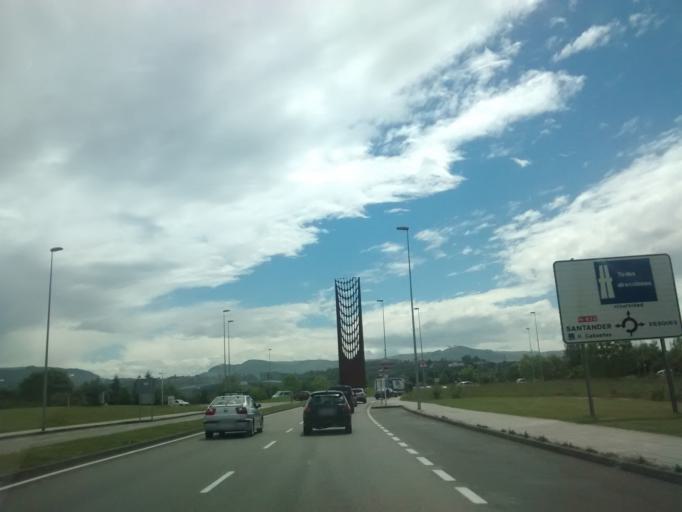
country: ES
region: Asturias
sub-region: Province of Asturias
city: Gijon
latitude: 43.5289
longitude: -5.6349
